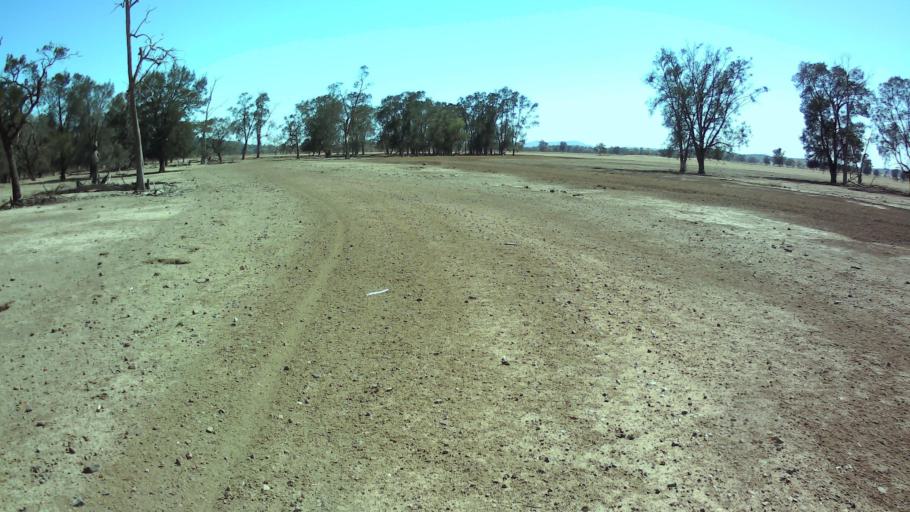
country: AU
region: New South Wales
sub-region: Bland
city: West Wyalong
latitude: -33.7584
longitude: 147.6590
